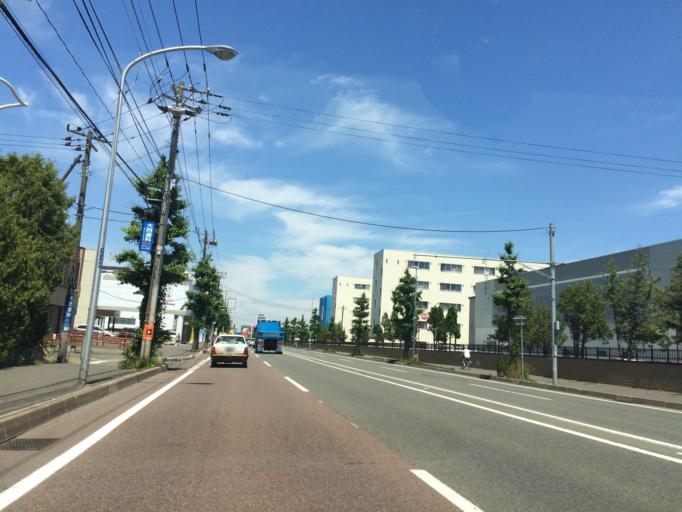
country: JP
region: Hokkaido
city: Sapporo
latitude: 43.0250
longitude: 141.3455
